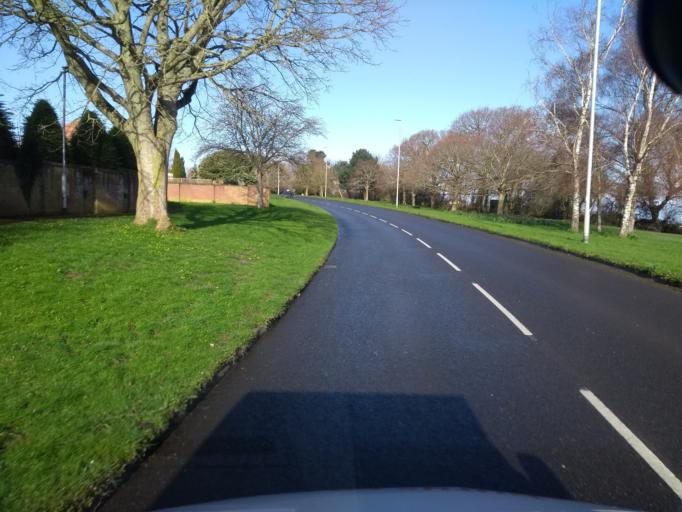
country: GB
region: England
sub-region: Somerset
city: Yeovil
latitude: 50.9590
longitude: -2.6124
